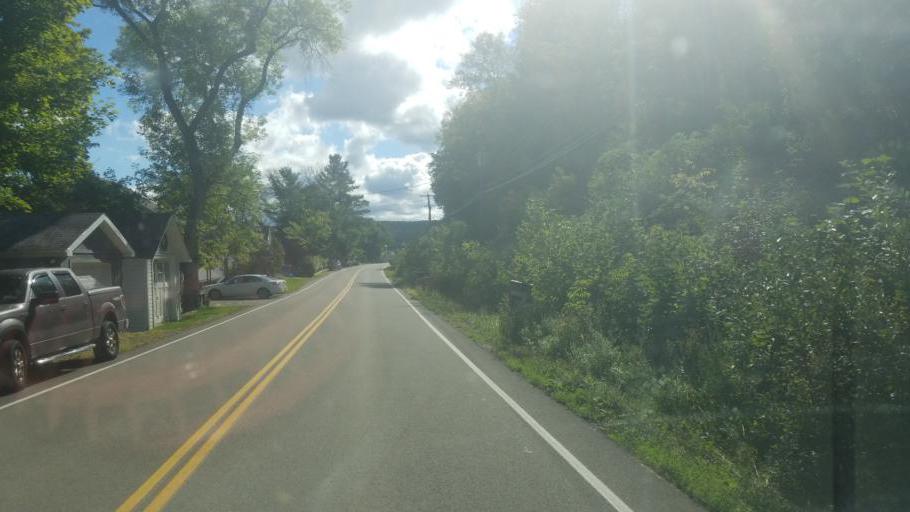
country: US
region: New York
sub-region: Allegany County
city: Cuba
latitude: 42.2480
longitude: -78.2832
